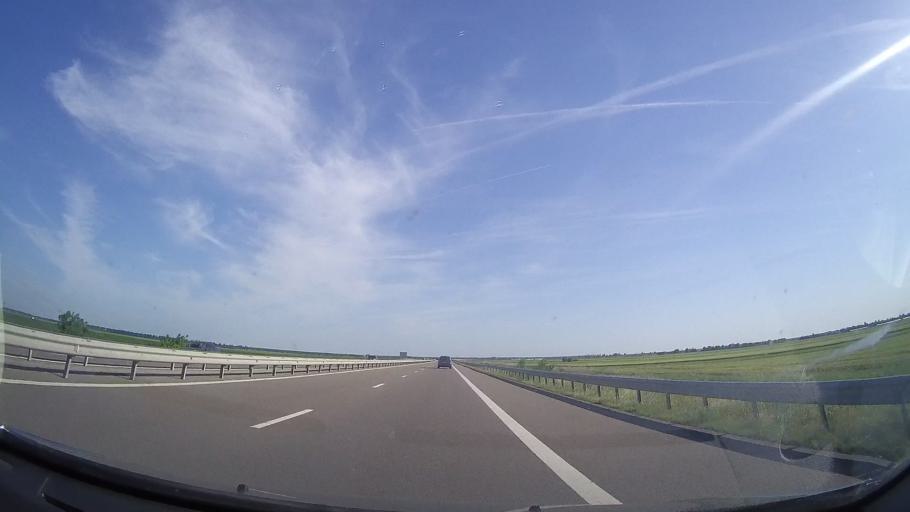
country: RO
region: Ilfov
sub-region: Comuna Gruiu
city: Gruiu
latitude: 44.7489
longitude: 26.2563
